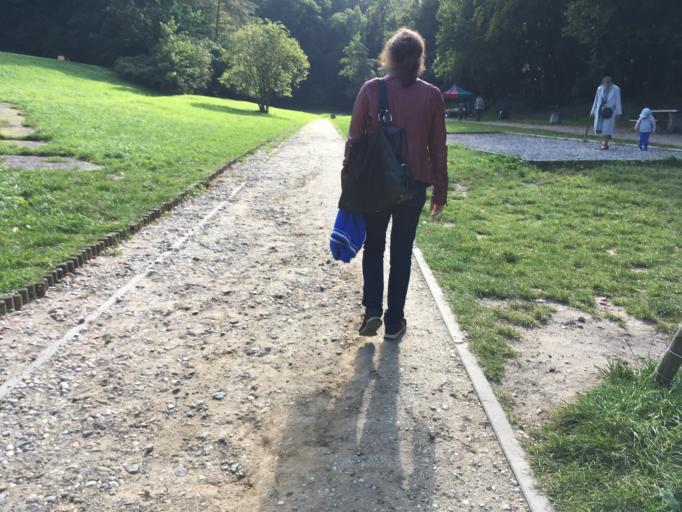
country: PL
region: Pomeranian Voivodeship
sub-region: Gdansk
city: Gdansk
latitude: 54.3750
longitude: 18.5936
